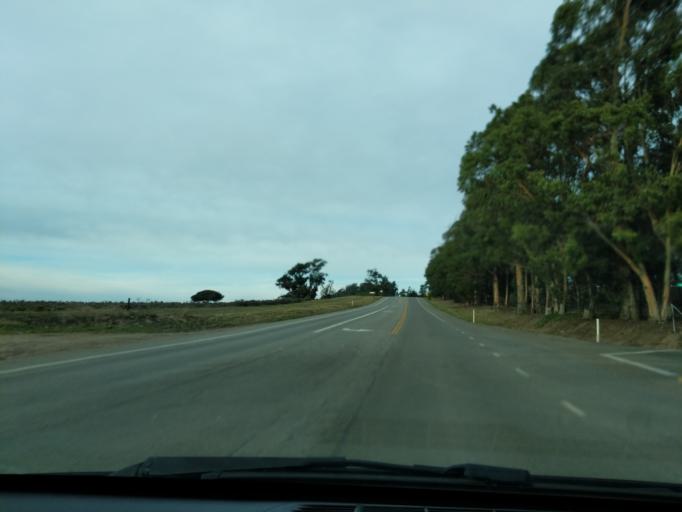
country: US
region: California
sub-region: San Luis Obispo County
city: Callender
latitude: 35.0228
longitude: -120.5626
